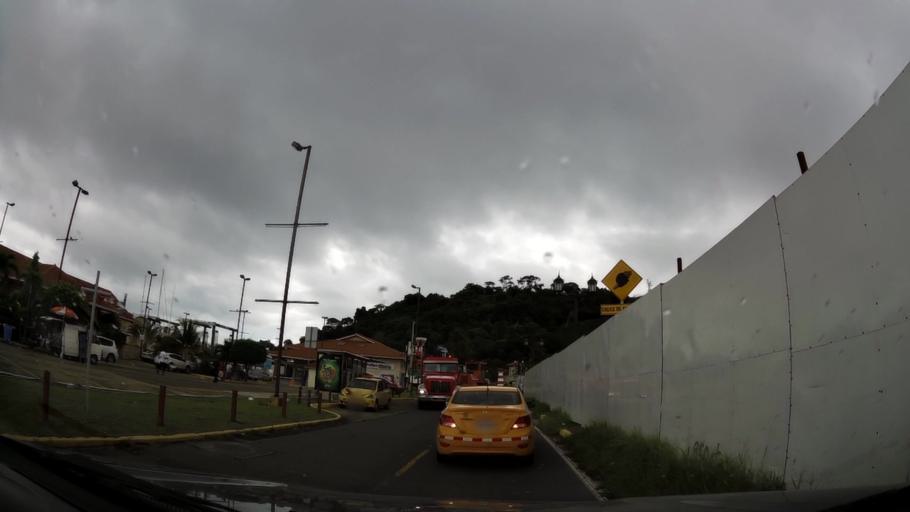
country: PA
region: Panama
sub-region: Distrito de Panama
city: Ancon
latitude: 8.9108
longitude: -79.5225
